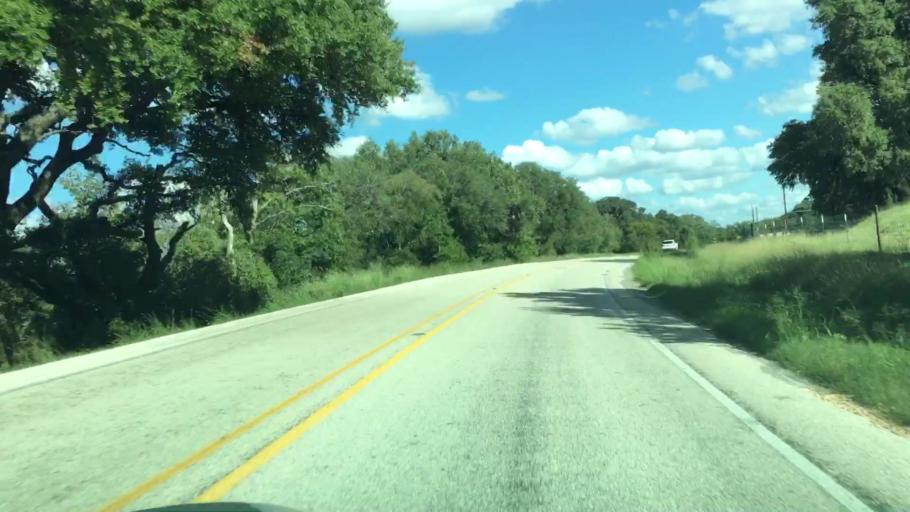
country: US
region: Texas
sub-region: Blanco County
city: Blanco
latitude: 30.0931
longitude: -98.4078
